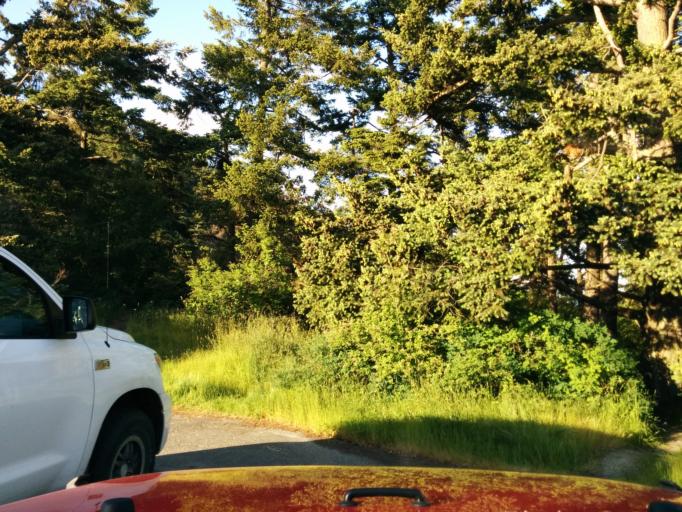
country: US
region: Washington
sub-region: Island County
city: Ault Field
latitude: 48.4078
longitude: -122.6445
